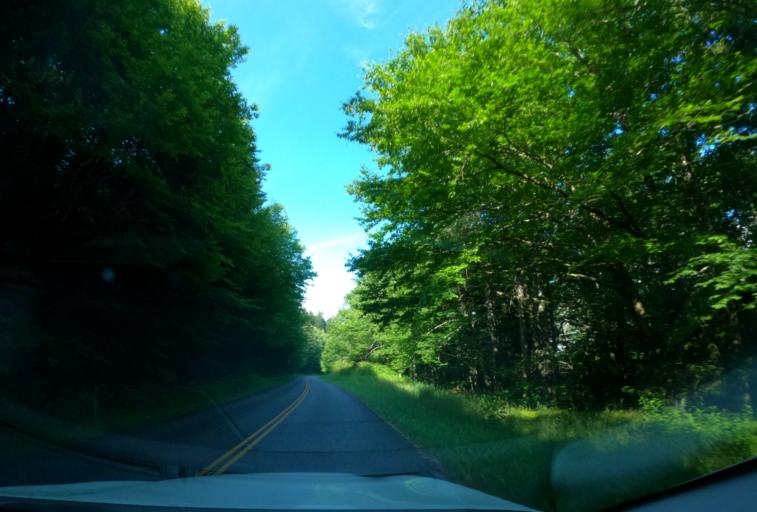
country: US
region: North Carolina
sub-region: Haywood County
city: Hazelwood
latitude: 35.3077
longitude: -82.9470
